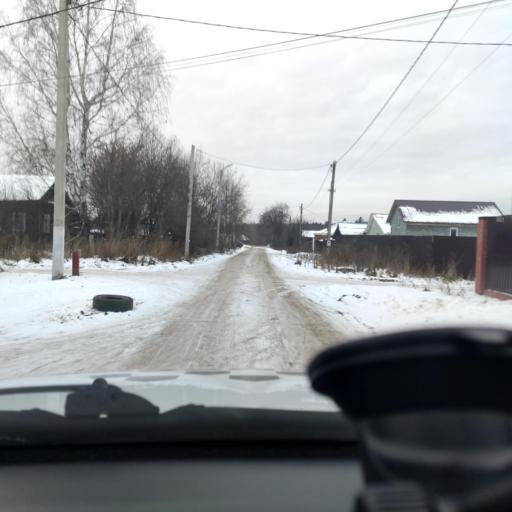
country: RU
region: Perm
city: Froly
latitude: 57.9548
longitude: 56.2890
